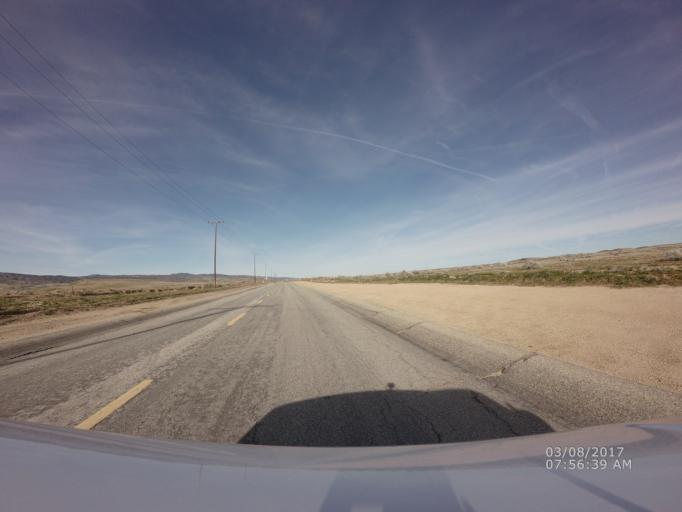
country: US
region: California
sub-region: Los Angeles County
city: Green Valley
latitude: 34.7248
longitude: -118.3910
